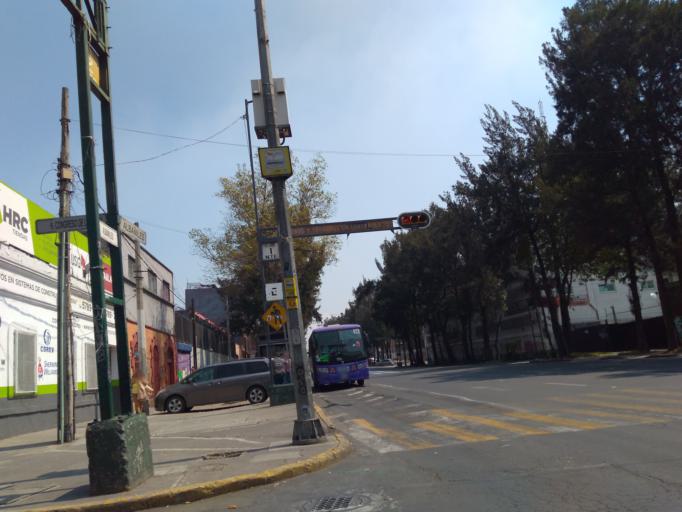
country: MX
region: Mexico City
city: Mexico City
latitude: 19.4383
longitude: -99.1183
